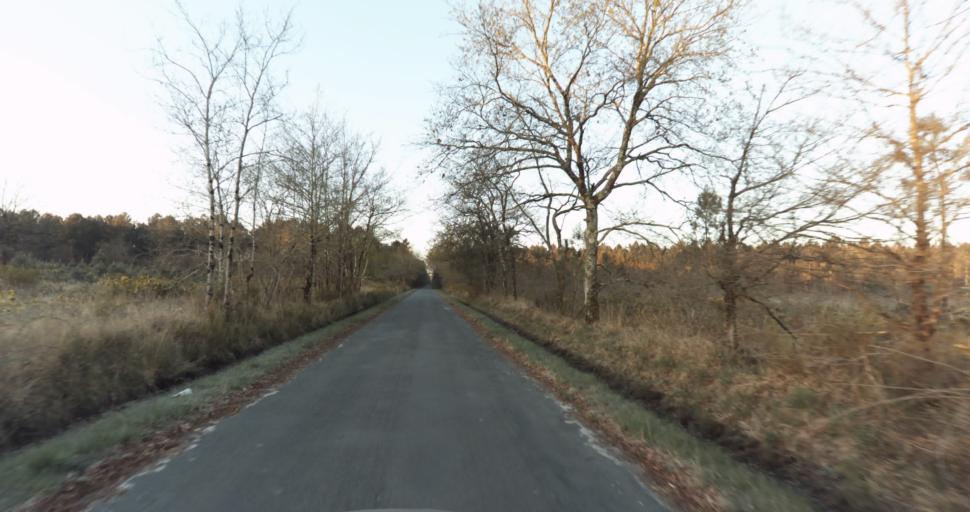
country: FR
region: Aquitaine
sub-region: Departement de la Gironde
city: Martignas-sur-Jalle
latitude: 44.8279
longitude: -0.7395
